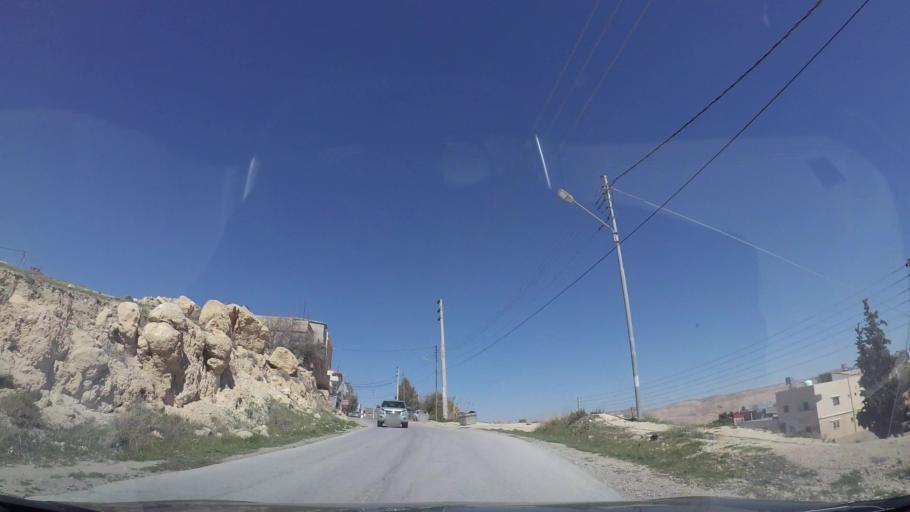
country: JO
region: Tafielah
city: At Tafilah
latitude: 30.8213
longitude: 35.5816
